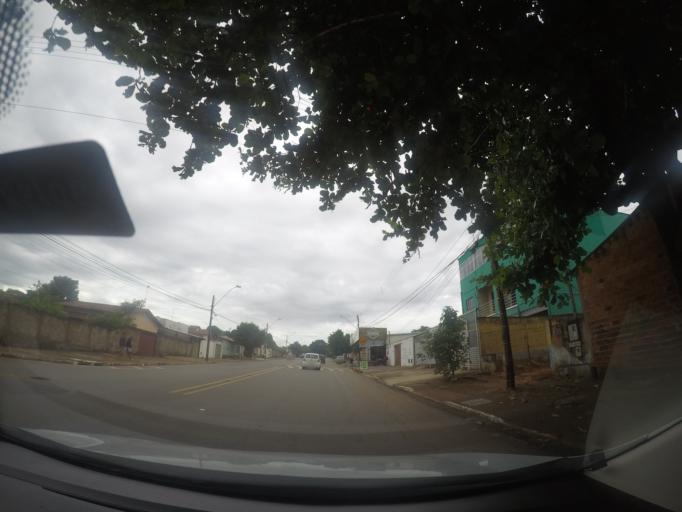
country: BR
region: Goias
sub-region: Goiania
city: Goiania
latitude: -16.6110
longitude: -49.2952
